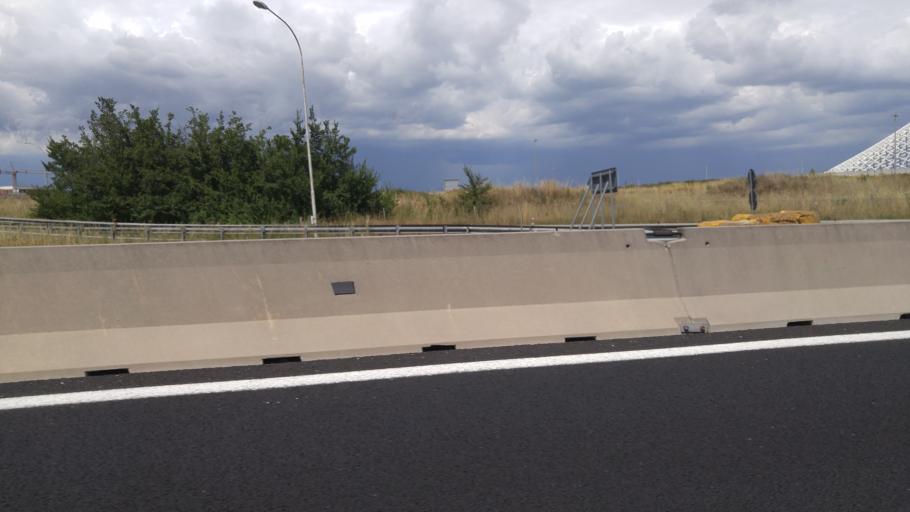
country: IT
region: Latium
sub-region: Citta metropolitana di Roma Capitale
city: Frascati
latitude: 41.8415
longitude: 12.6294
